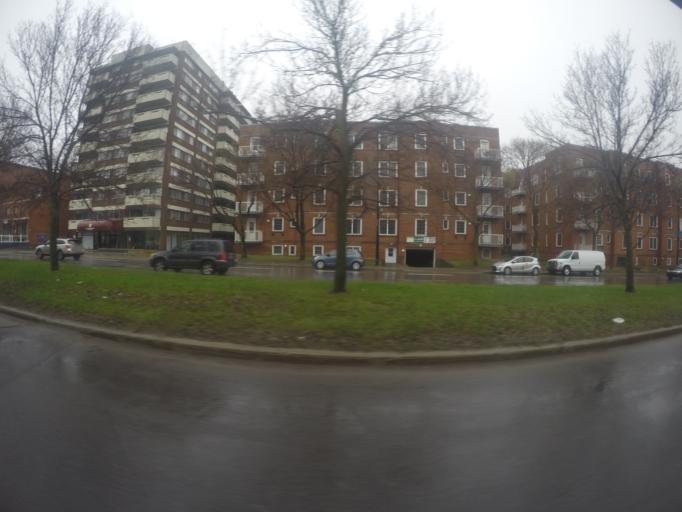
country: CA
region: Quebec
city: Montreal-Ouest
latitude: 45.4128
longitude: -73.6571
